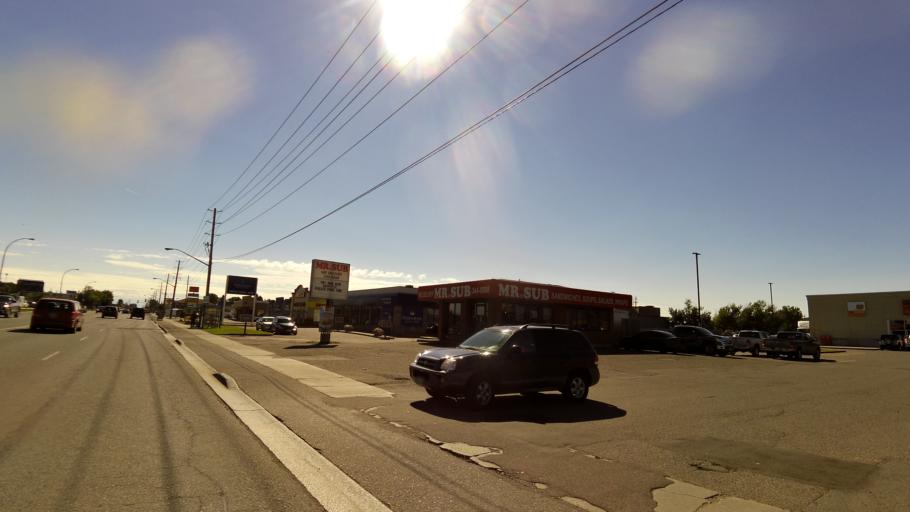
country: CA
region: Ontario
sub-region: Thunder Bay District
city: Thunder Bay
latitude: 48.3808
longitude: -89.2935
